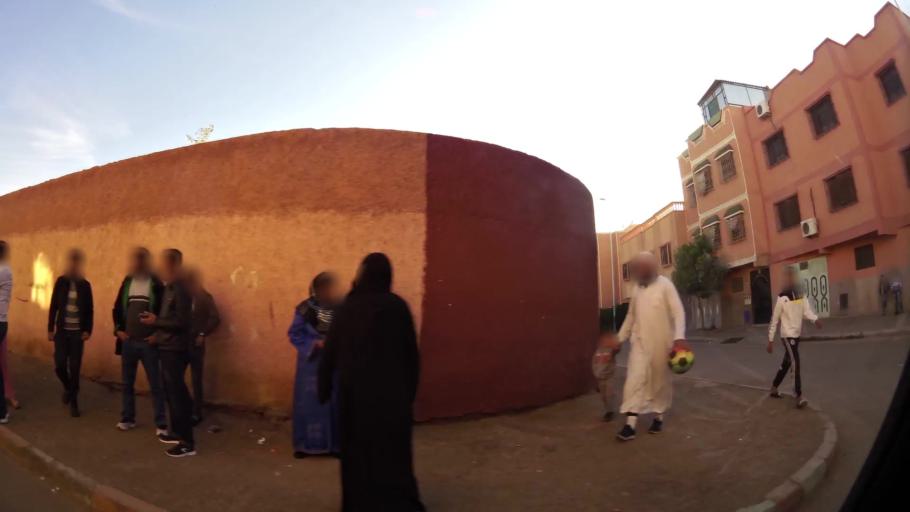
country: MA
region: Marrakech-Tensift-Al Haouz
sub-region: Marrakech
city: Marrakesh
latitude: 31.6189
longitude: -8.0678
